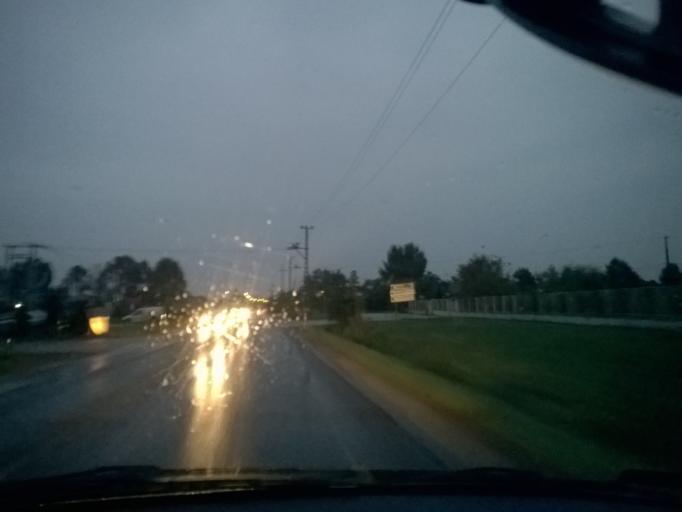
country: HU
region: Budapest
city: Budapest XXII. keruelet
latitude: 47.3858
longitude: 19.0503
